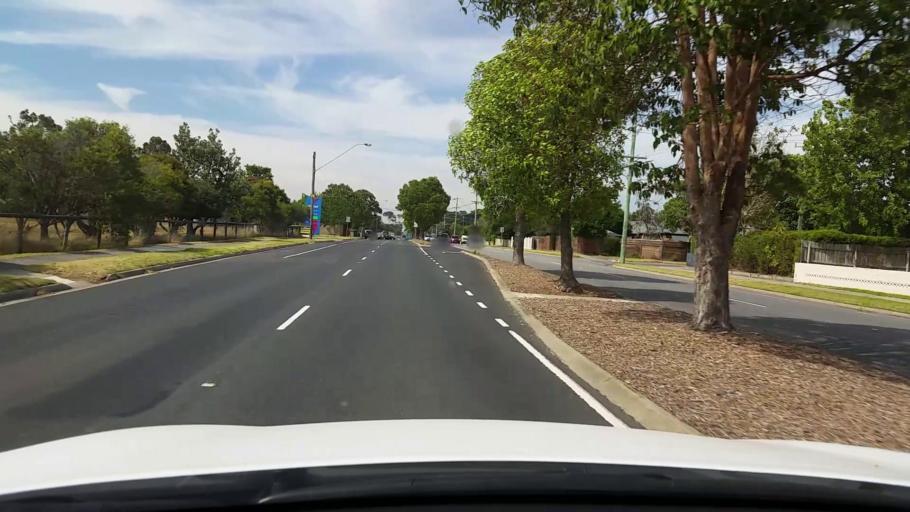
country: AU
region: Victoria
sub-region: Mornington Peninsula
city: Tyabb
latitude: -38.2572
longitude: 145.1898
